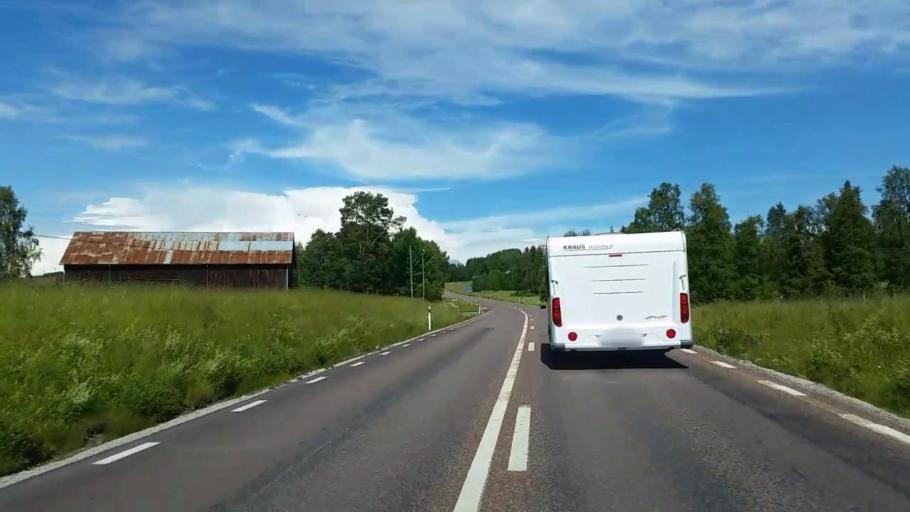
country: SE
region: Dalarna
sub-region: Rattviks Kommun
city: Raettvik
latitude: 60.9976
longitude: 15.2183
